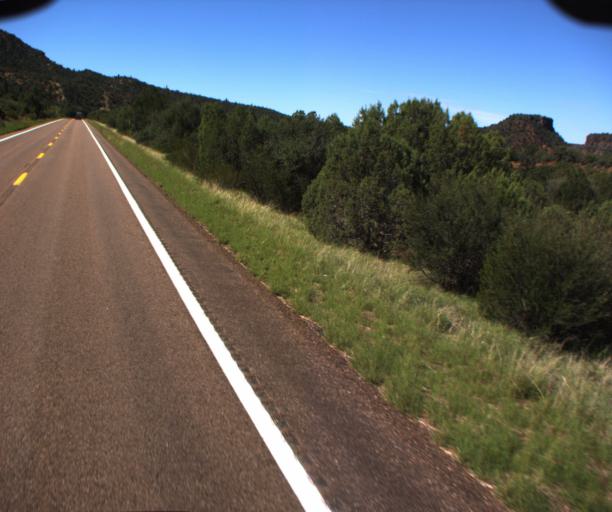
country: US
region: Arizona
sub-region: Navajo County
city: Cibecue
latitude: 34.0196
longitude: -110.2396
